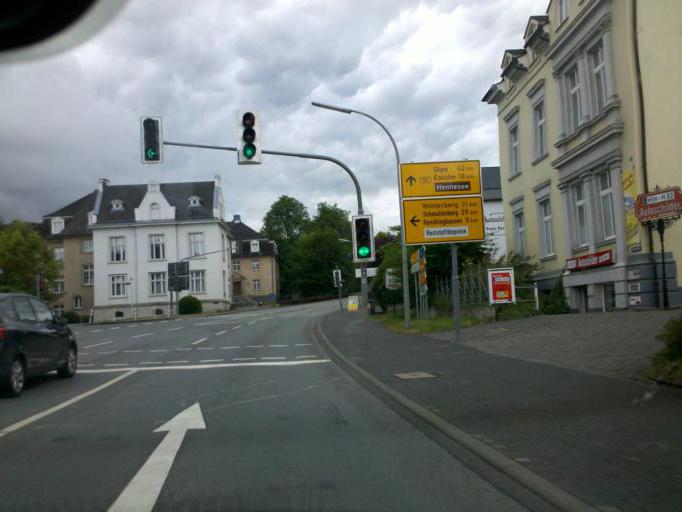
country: DE
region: North Rhine-Westphalia
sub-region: Regierungsbezirk Arnsberg
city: Meschede
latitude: 51.3424
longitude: 8.2828
